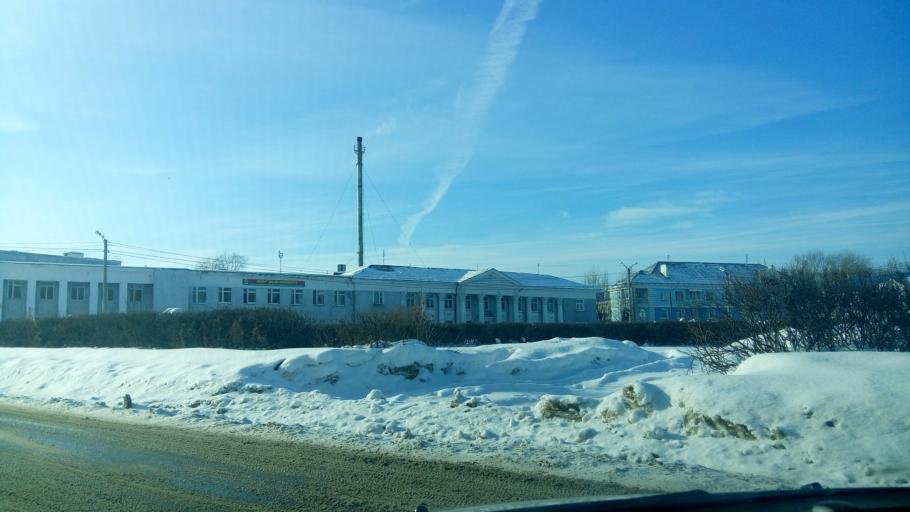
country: RU
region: Sverdlovsk
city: Bogdanovich
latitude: 56.7733
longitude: 62.0570
